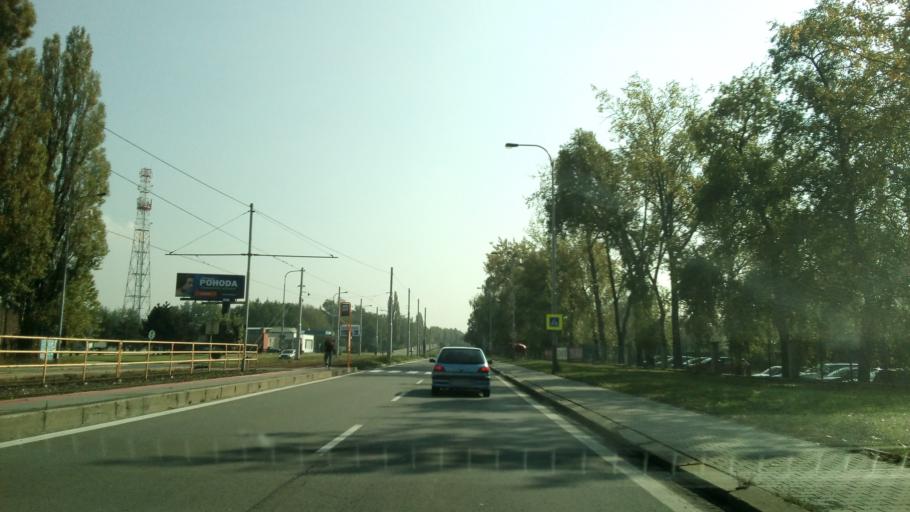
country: CZ
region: Moravskoslezsky
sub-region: Okres Ostrava-Mesto
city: Ostrava
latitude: 49.8143
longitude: 18.2393
